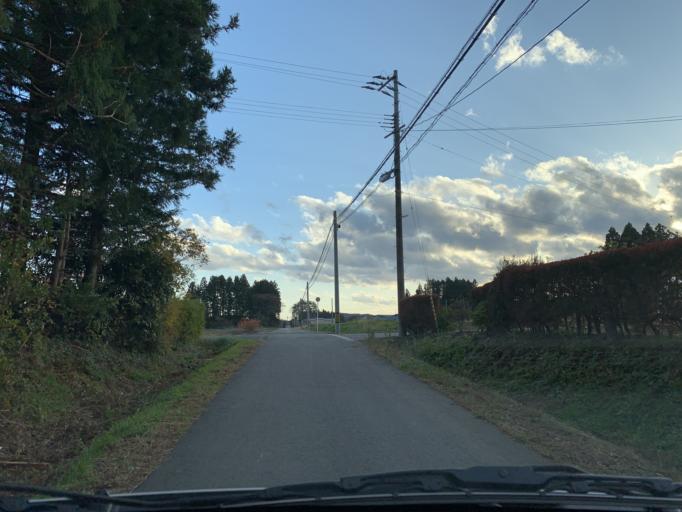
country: JP
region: Iwate
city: Mizusawa
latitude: 39.0924
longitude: 141.0377
